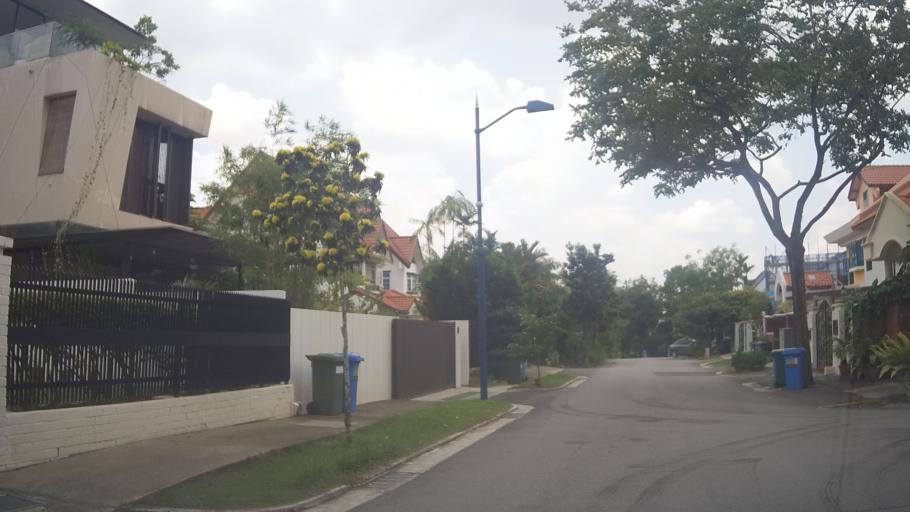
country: SG
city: Singapore
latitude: 1.3645
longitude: 103.8710
